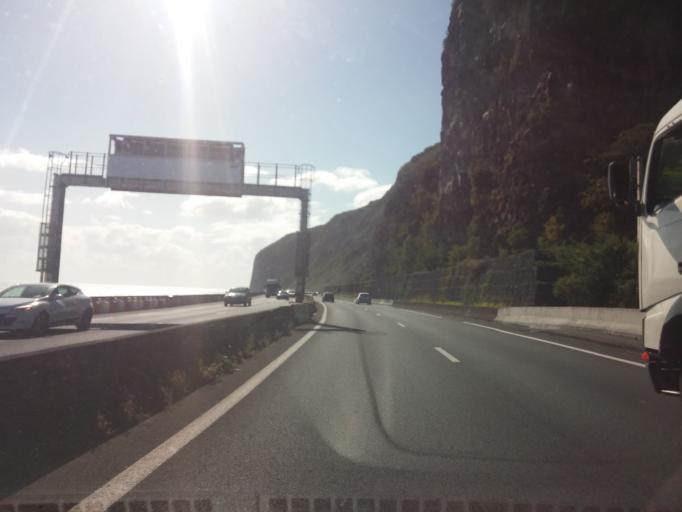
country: RE
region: Reunion
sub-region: Reunion
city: La Possession
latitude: -20.8910
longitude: 55.3848
